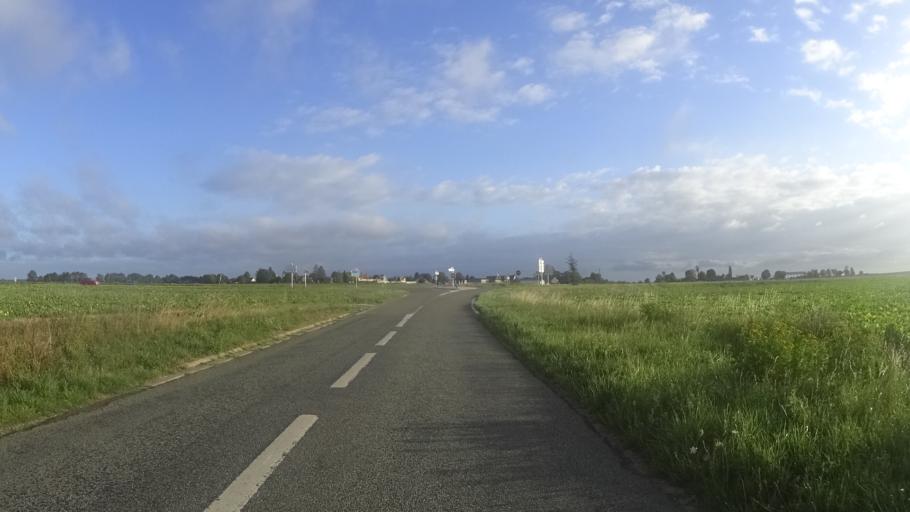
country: FR
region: Picardie
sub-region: Departement de l'Oise
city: Chamant
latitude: 49.2146
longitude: 2.6660
